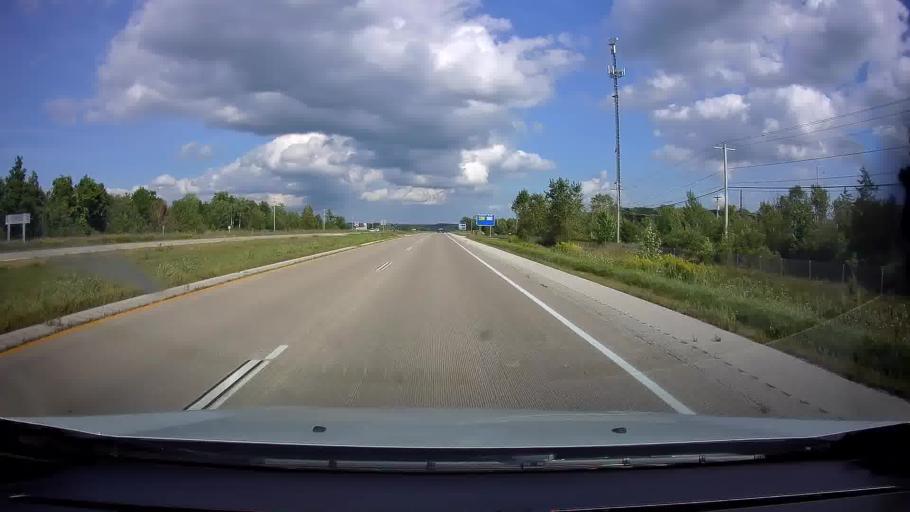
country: US
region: Wisconsin
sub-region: Kewaunee County
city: Luxemburg
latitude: 44.6336
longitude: -87.7928
